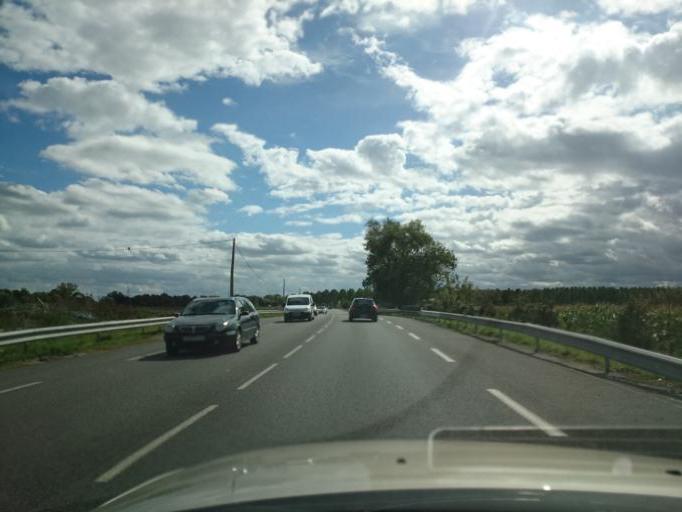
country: FR
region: Aquitaine
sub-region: Departement de la Gironde
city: Saint-Louis-de-Montferrand
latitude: 44.9386
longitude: -0.5618
